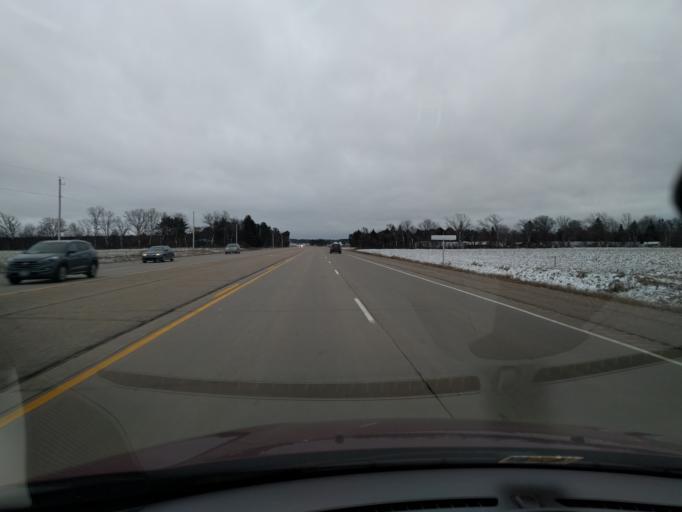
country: US
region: Wisconsin
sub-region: Portage County
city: Whiting
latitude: 44.5225
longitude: -89.4746
